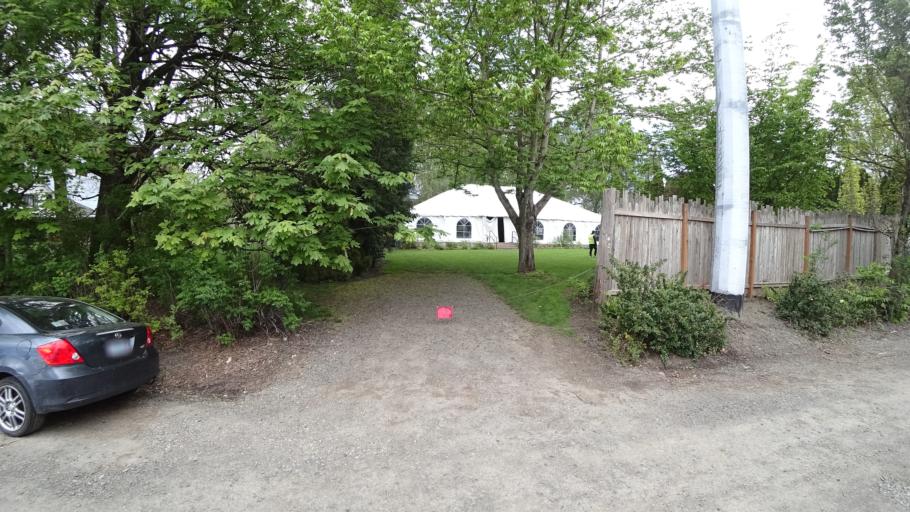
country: US
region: Oregon
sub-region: Washington County
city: Rockcreek
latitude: 45.5485
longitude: -122.9006
